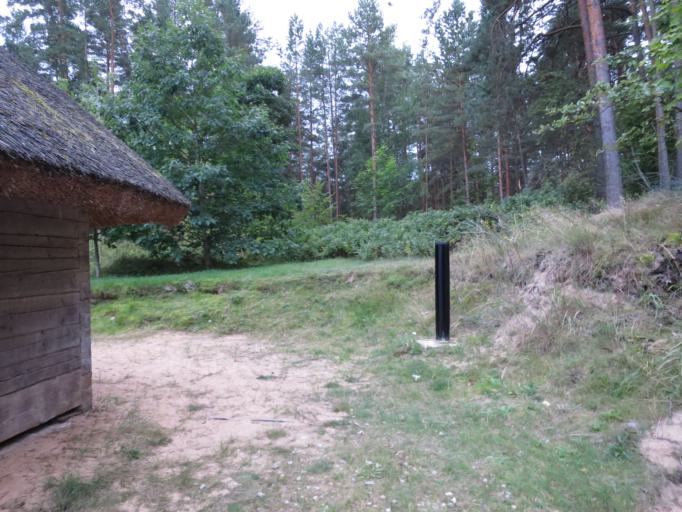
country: LV
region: Riga
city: Bergi
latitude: 56.9931
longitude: 24.2738
